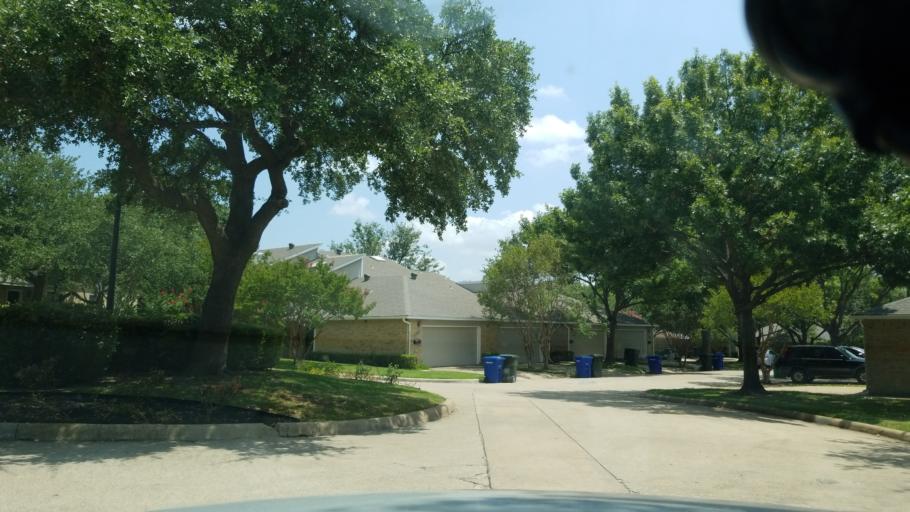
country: US
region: Texas
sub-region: Dallas County
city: Addison
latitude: 32.9692
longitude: -96.8607
